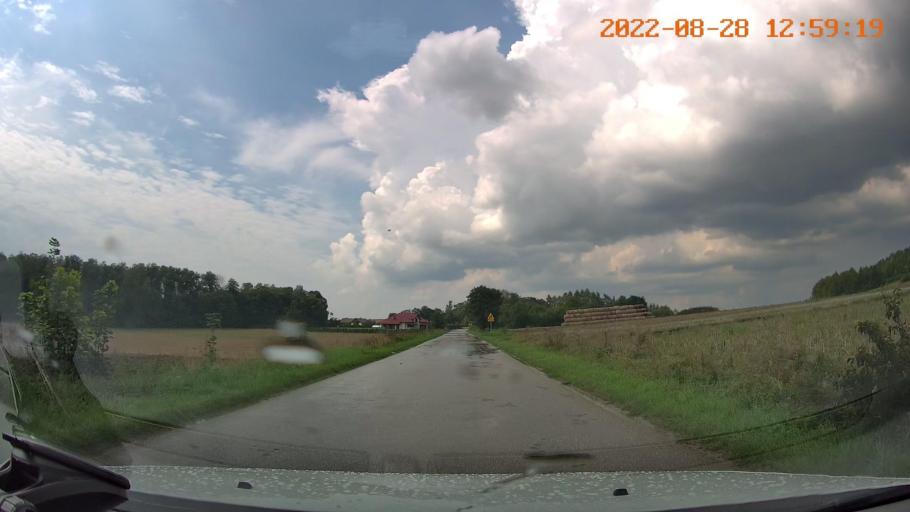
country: PL
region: Lesser Poland Voivodeship
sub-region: Powiat miechowski
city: Miechow
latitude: 50.3591
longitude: 20.1664
